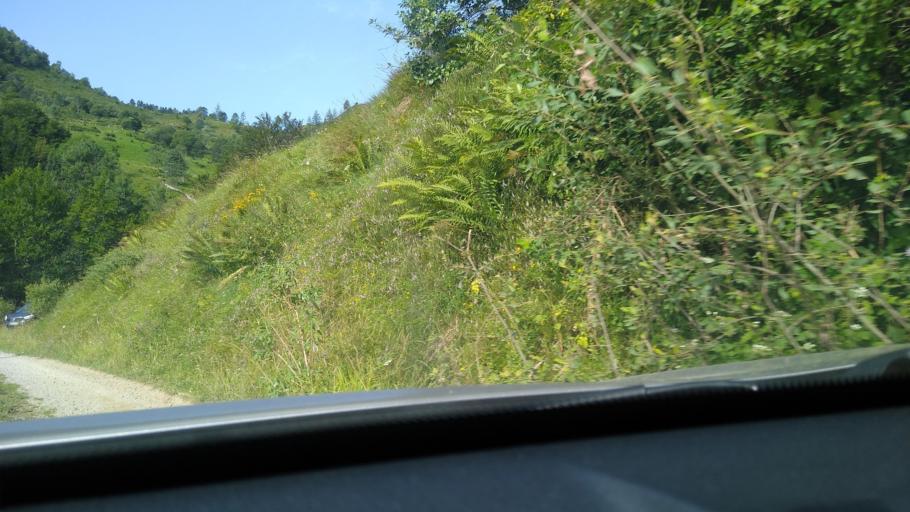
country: FR
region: Midi-Pyrenees
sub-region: Departement de l'Ariege
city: Saint-Girons
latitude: 42.7912
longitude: 1.1485
